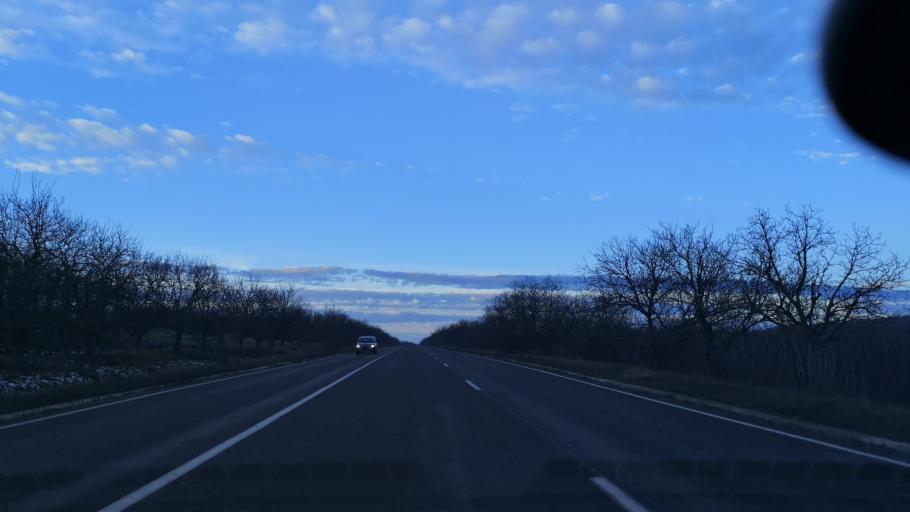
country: MD
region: Orhei
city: Orhei
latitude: 47.5112
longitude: 28.8007
